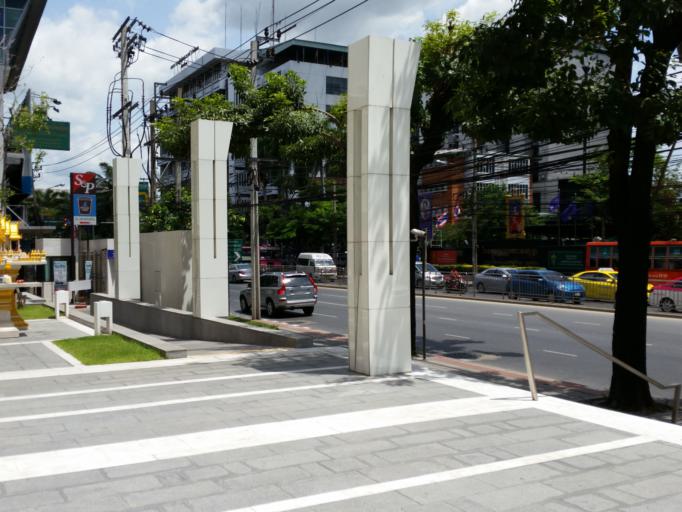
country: TH
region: Bangkok
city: Ratchathewi
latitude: 13.7665
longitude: 100.5343
